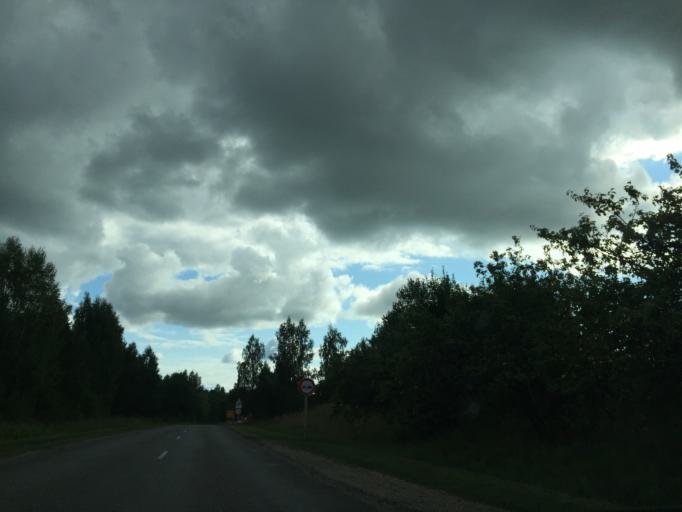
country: LV
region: Limbazu Rajons
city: Limbazi
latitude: 57.3565
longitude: 24.6684
